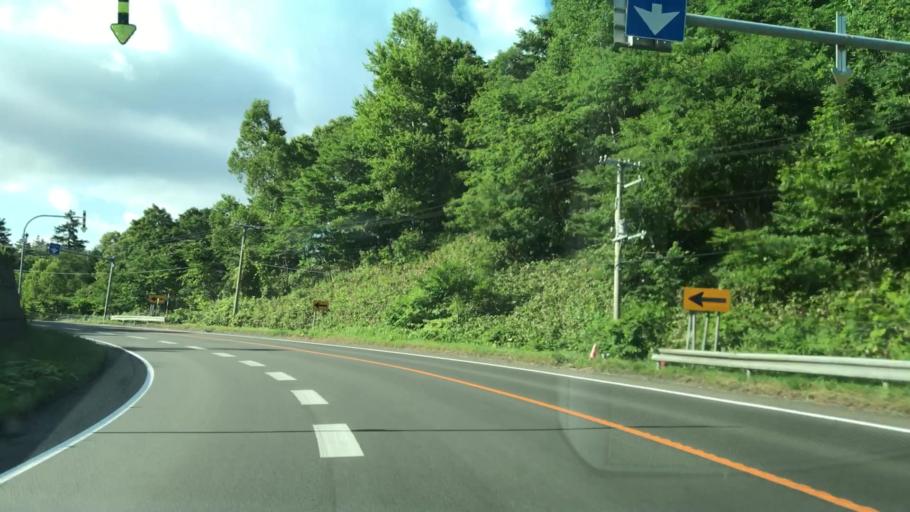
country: JP
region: Hokkaido
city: Shimo-furano
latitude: 42.9031
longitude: 142.4219
